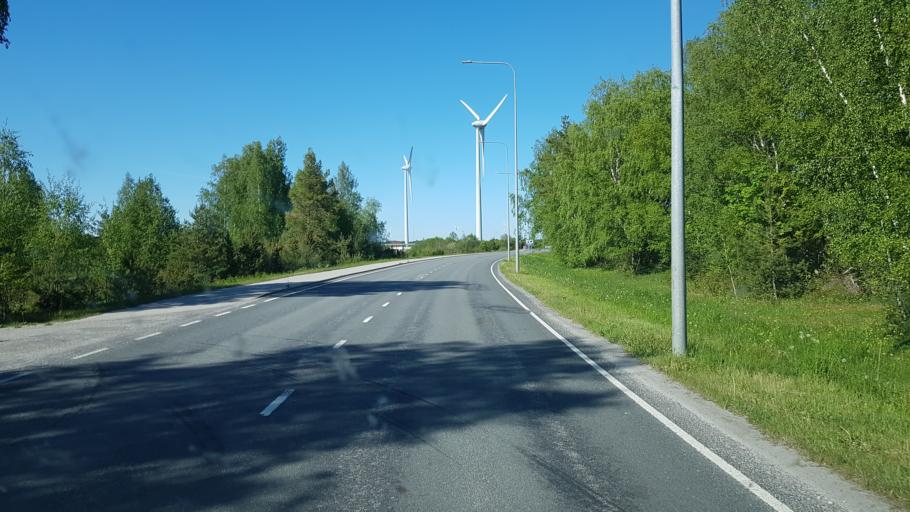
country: EE
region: Laeaene
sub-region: Lihula vald
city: Lihula
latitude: 58.5846
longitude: 23.5261
